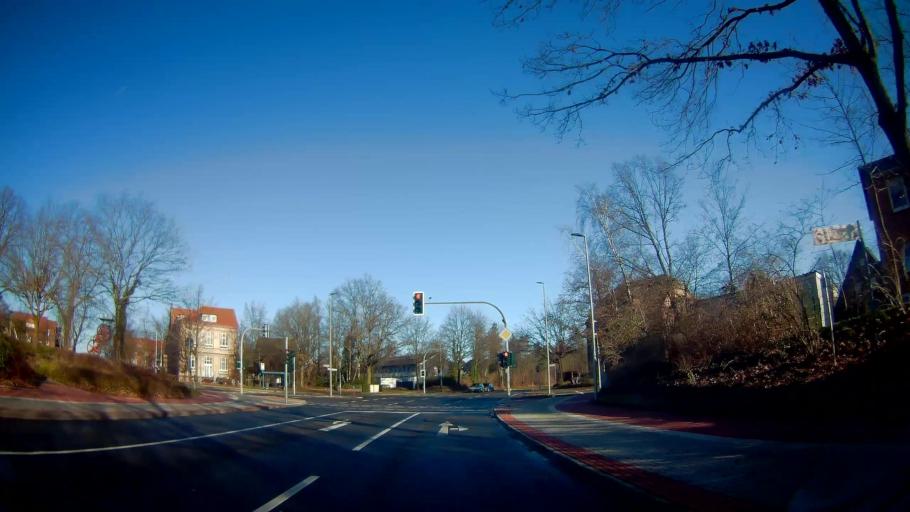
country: DE
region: North Rhine-Westphalia
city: Dorsten
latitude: 51.6740
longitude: 6.9733
